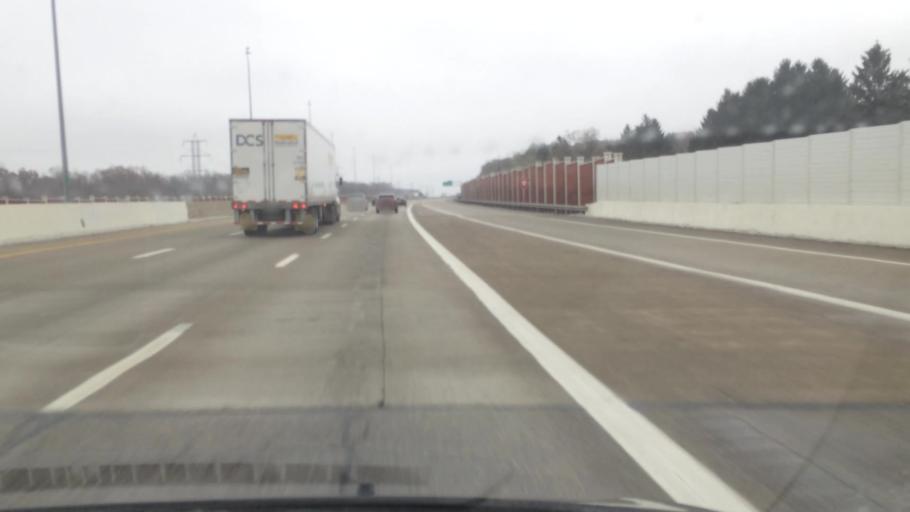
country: US
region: Ohio
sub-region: Cuyahoga County
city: Independence
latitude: 41.3586
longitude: -81.6498
